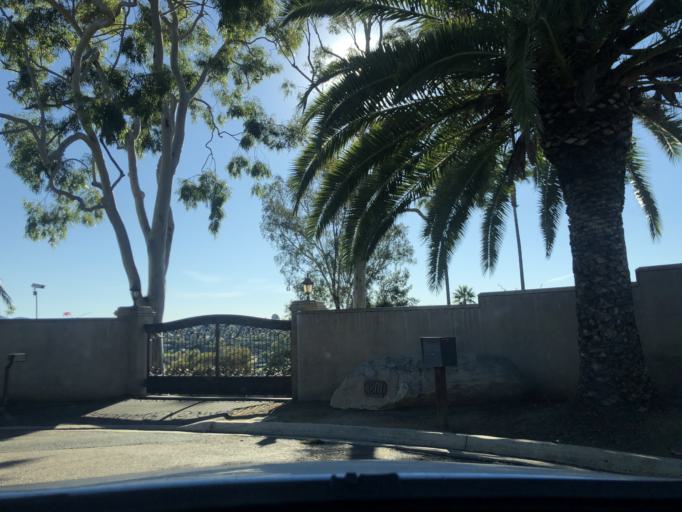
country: US
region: California
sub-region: San Diego County
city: El Cajon
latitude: 32.7818
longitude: -116.9414
